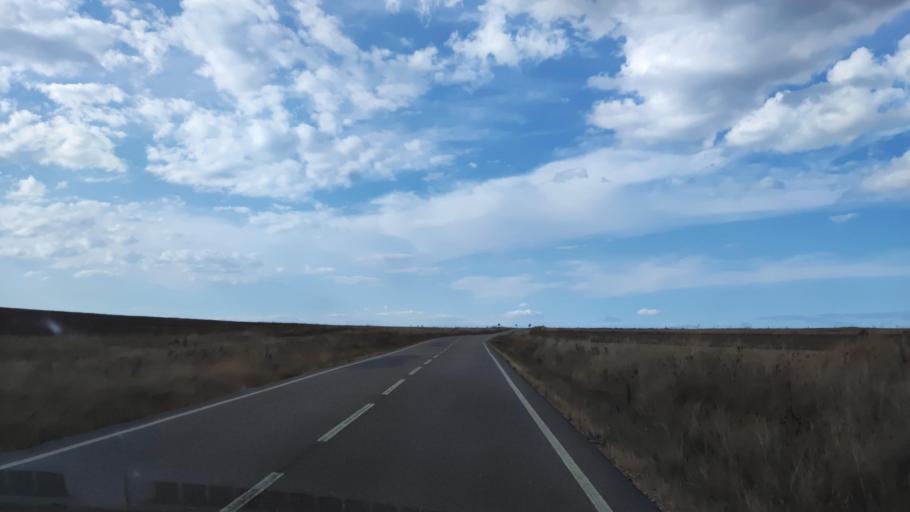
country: ES
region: Castille and Leon
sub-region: Provincia de Salamanca
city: Pastores
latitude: 40.5077
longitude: -6.5045
